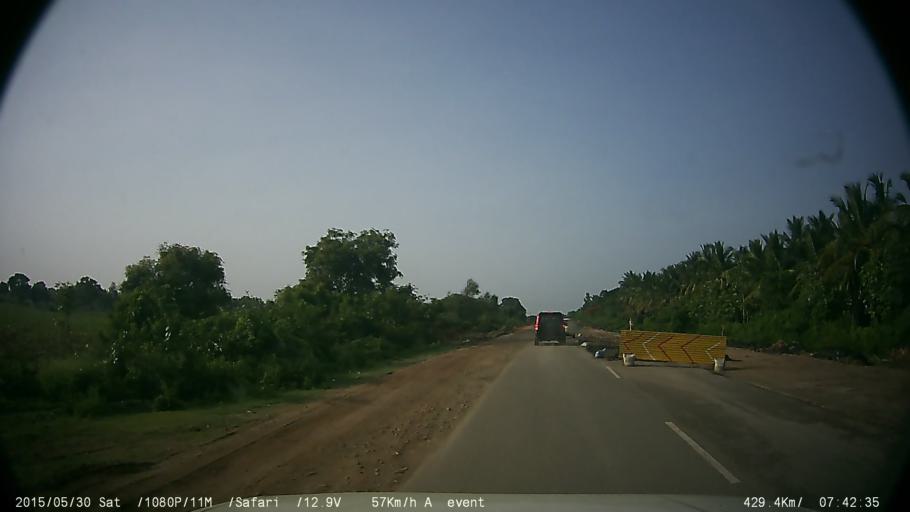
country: IN
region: Karnataka
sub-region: Chamrajnagar
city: Gundlupet
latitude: 11.9164
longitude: 76.6709
